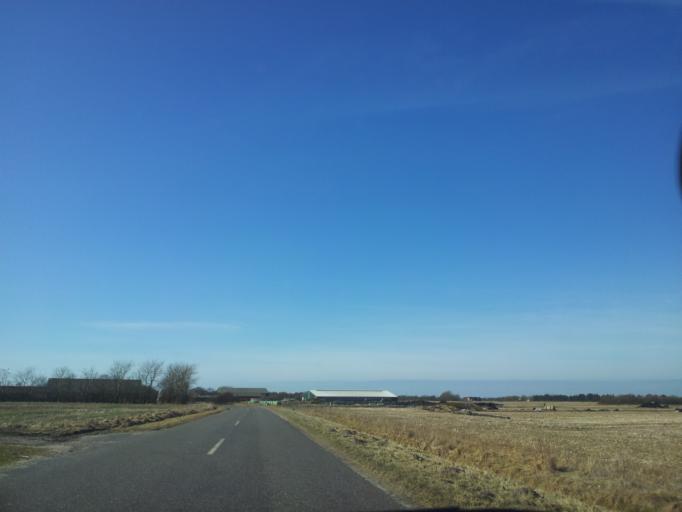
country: DK
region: South Denmark
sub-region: Tonder Kommune
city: Sherrebek
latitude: 55.1724
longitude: 8.7296
